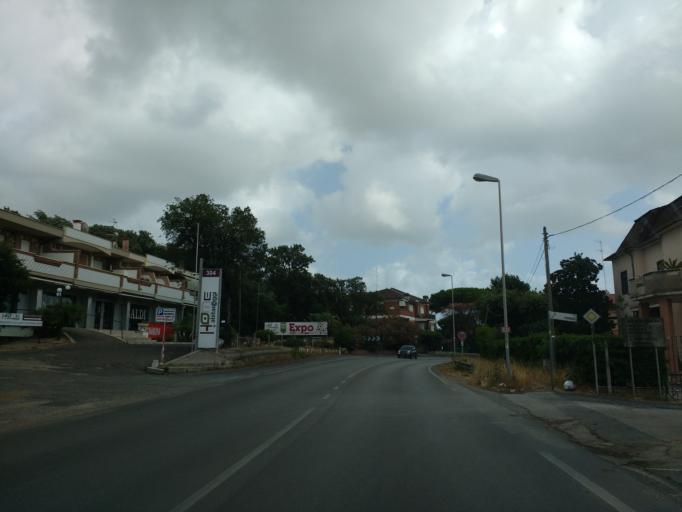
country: IT
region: Latium
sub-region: Citta metropolitana di Roma Capitale
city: Anzio
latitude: 41.4813
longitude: 12.6039
